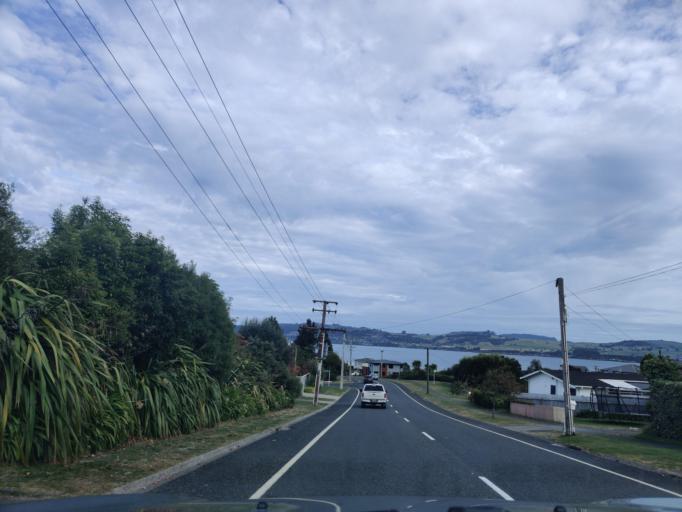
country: NZ
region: Waikato
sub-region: Taupo District
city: Taupo
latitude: -38.7083
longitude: 176.0934
